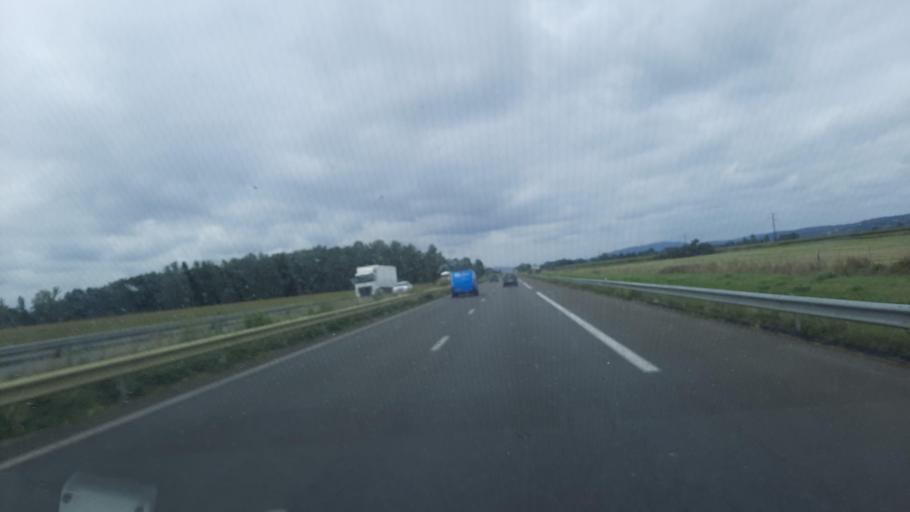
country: FR
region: Midi-Pyrenees
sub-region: Departement de la Haute-Garonne
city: Cazeres
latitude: 43.2503
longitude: 1.0977
